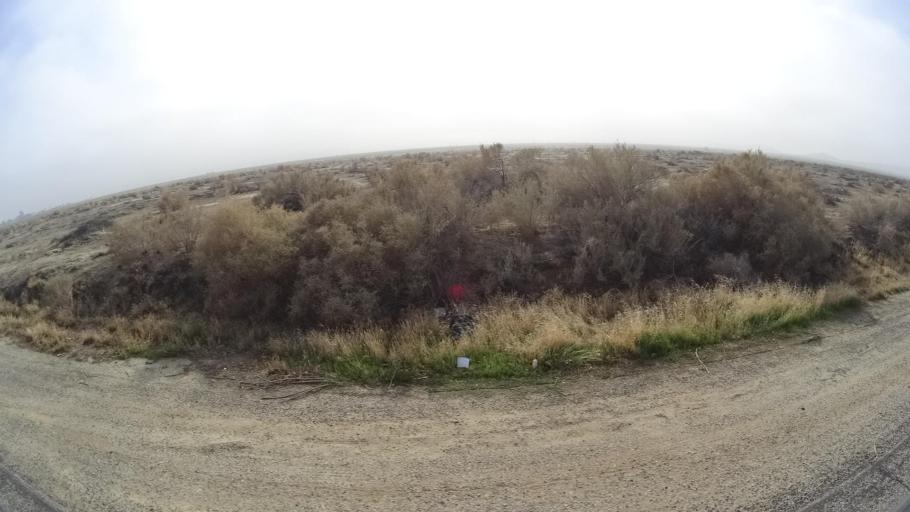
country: US
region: California
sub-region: Kern County
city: Ford City
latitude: 35.2096
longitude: -119.4219
